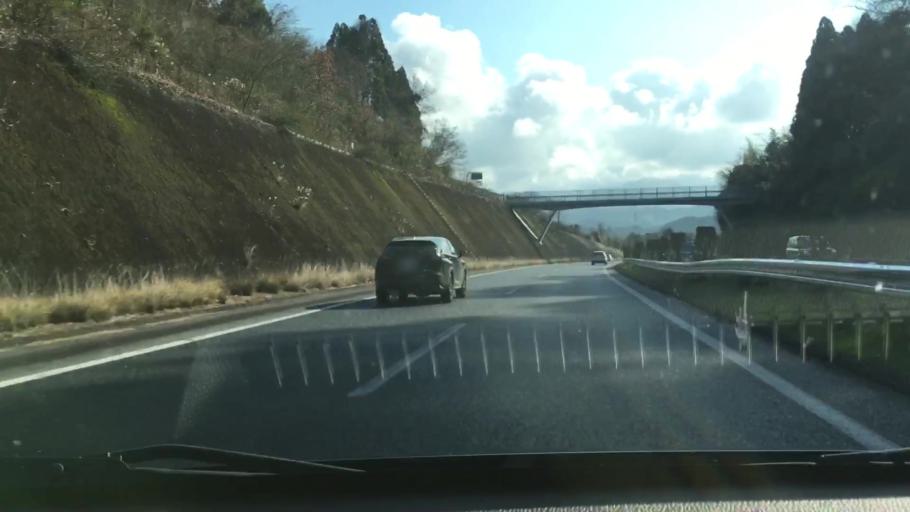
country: JP
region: Kumamoto
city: Matsubase
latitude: 32.5881
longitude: 130.7165
